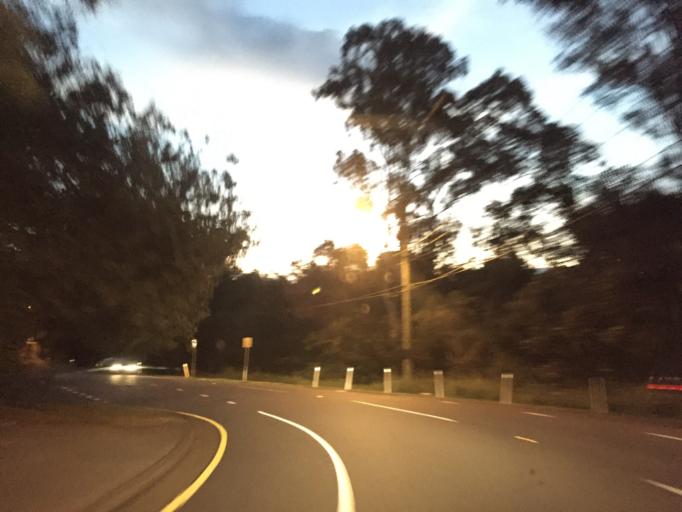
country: AU
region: Queensland
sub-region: Moreton Bay
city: Ferny Hills
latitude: -27.4487
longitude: 152.9443
